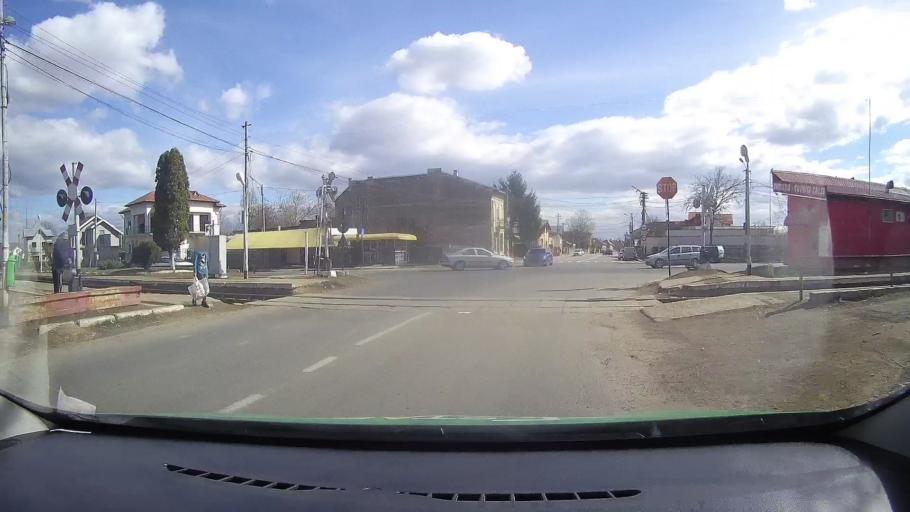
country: RO
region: Dambovita
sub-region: Municipiul Targoviste
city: Targoviste
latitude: 44.9404
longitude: 25.4434
